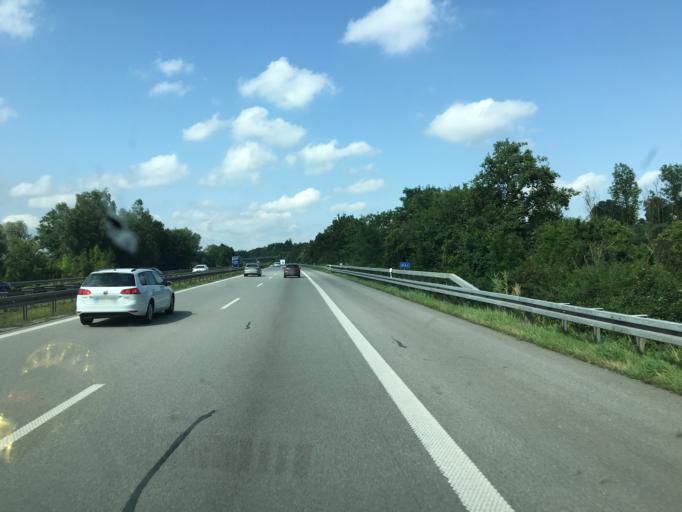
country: DE
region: Bavaria
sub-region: Lower Bavaria
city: Passau
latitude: 48.5134
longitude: 13.3933
